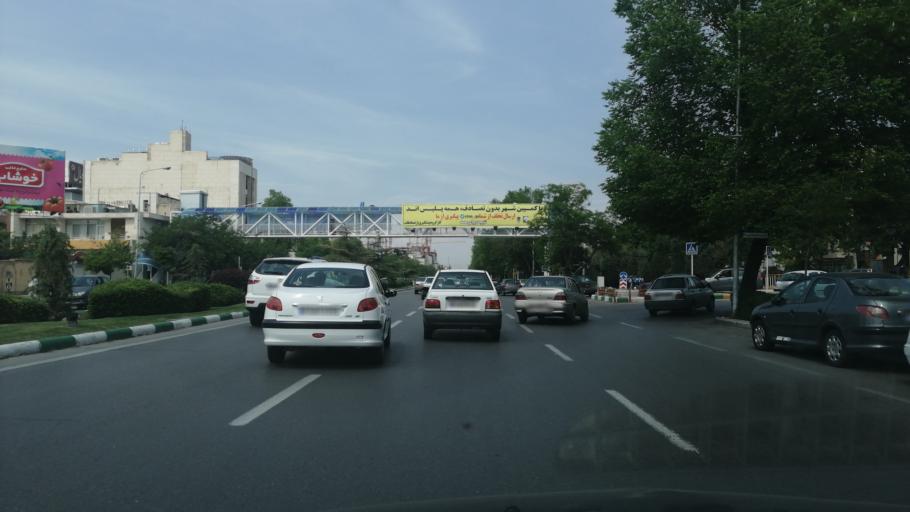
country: IR
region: Razavi Khorasan
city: Mashhad
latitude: 36.3098
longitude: 59.5549
